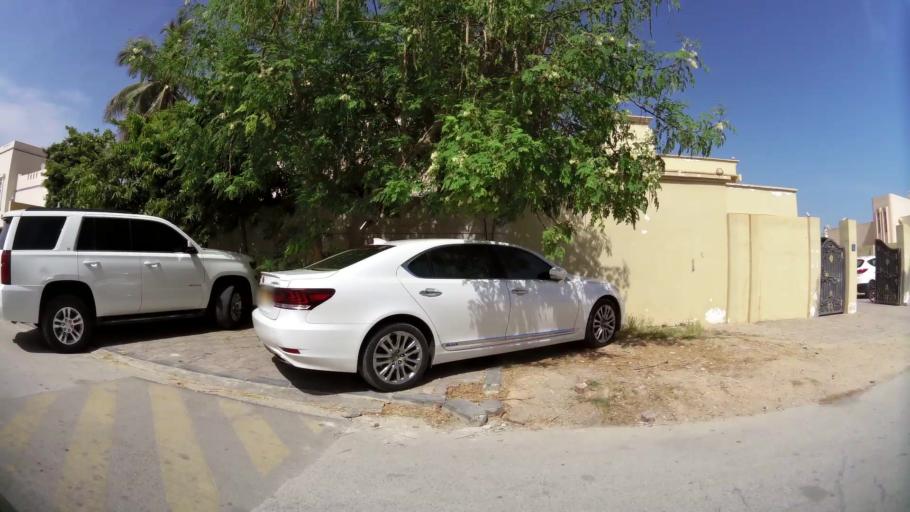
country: OM
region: Zufar
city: Salalah
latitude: 17.0490
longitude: 54.1502
